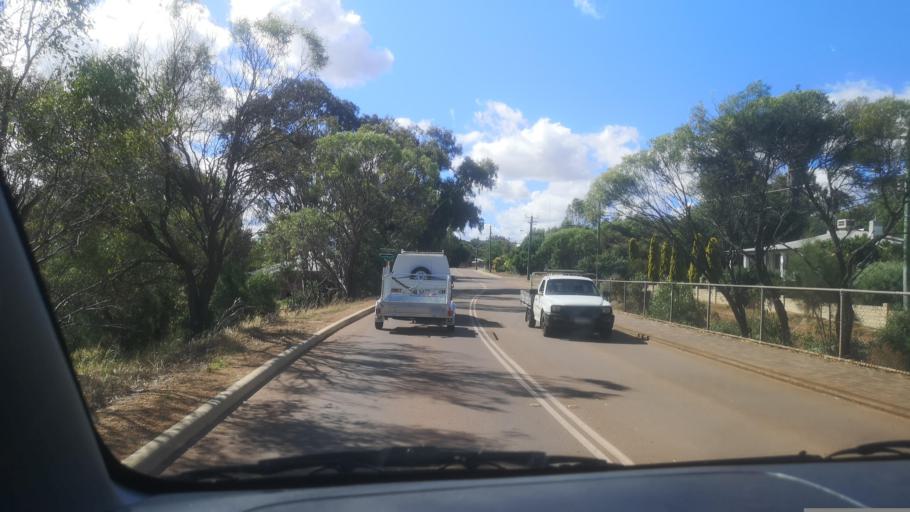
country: AU
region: Western Australia
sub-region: Toodyay
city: Toodyay
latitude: -31.5487
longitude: 116.4624
